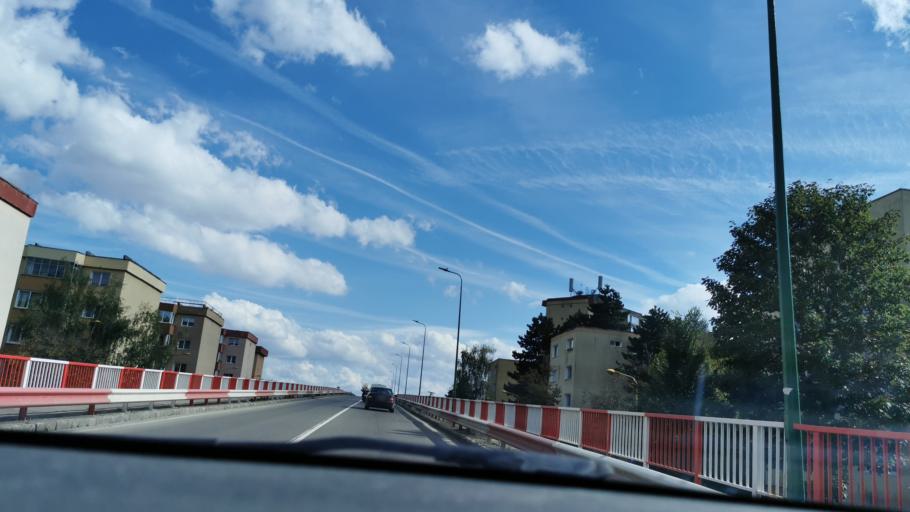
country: RO
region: Brasov
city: Brasov
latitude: 45.6493
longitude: 25.6325
